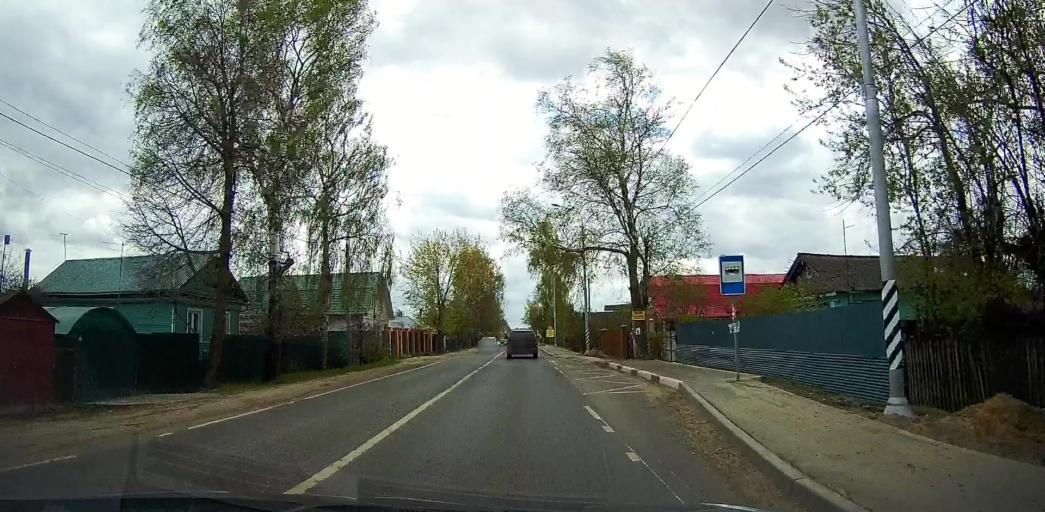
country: RU
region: Moskovskaya
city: Beloozerskiy
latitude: 55.4617
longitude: 38.4219
